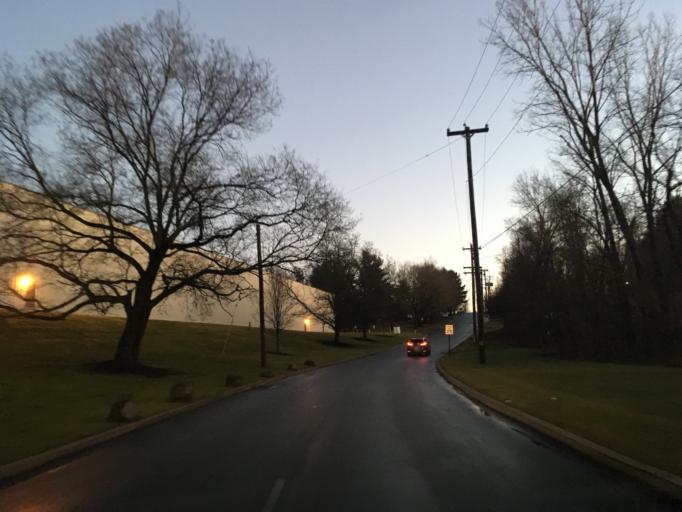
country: US
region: Pennsylvania
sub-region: Delaware County
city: Chester Heights
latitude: 39.8907
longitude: -75.5303
